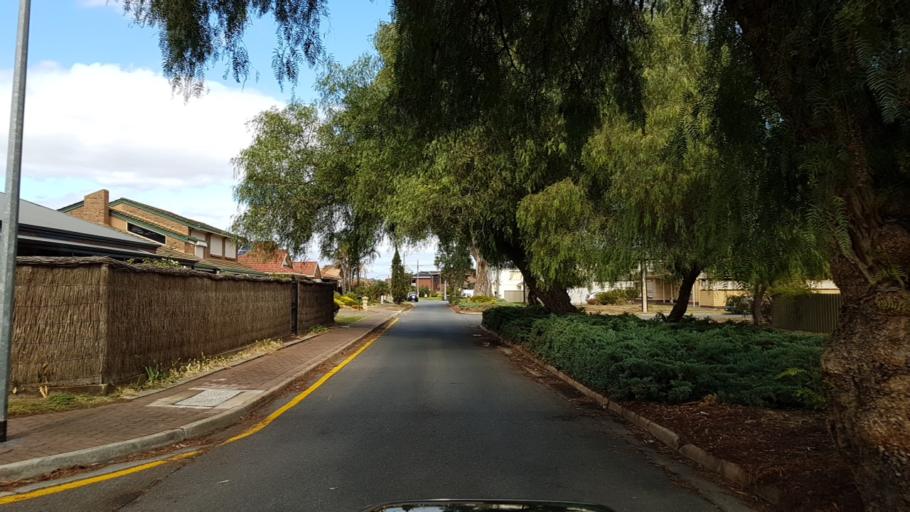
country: AU
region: South Australia
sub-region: Charles Sturt
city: Seaton
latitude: -34.9068
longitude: 138.5176
